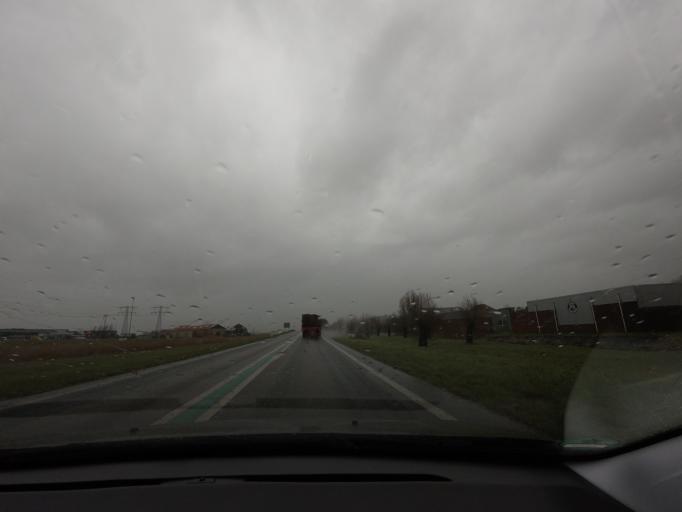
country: NL
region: Friesland
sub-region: Sudwest Fryslan
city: Bolsward
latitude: 53.0660
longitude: 5.5096
